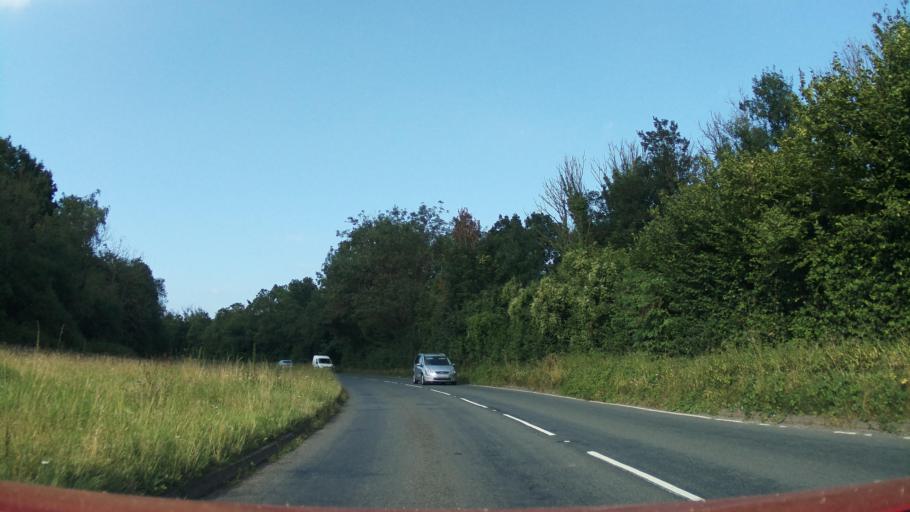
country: GB
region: England
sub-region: Devon
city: Tiverton
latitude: 50.8780
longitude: -3.4908
